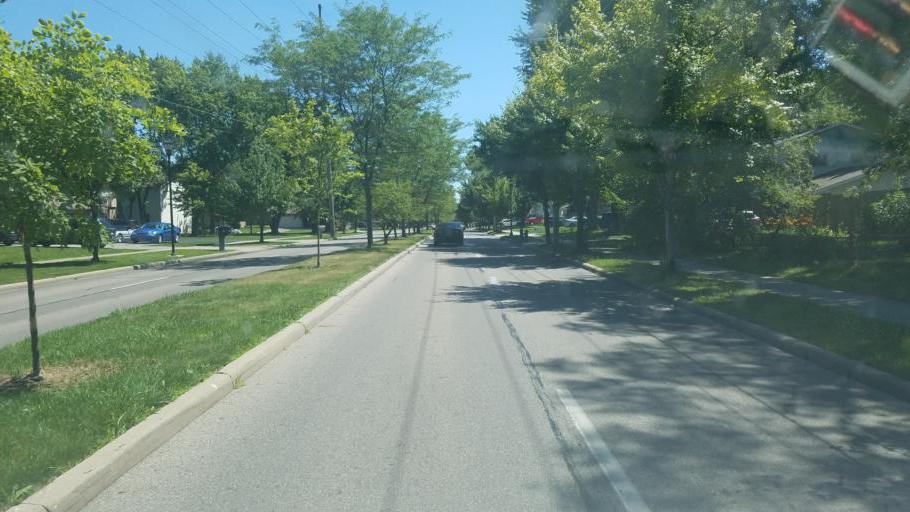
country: US
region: Ohio
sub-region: Franklin County
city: Westerville
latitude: 40.1292
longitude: -82.9032
